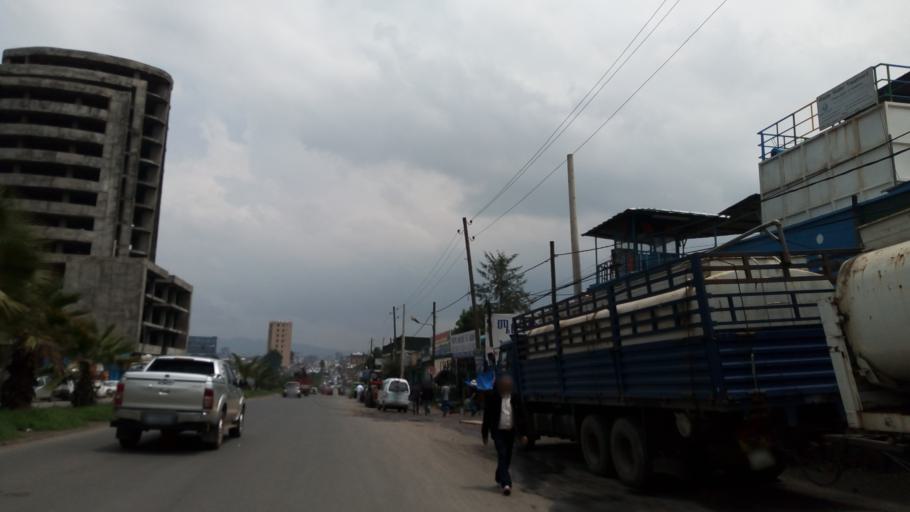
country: ET
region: Adis Abeba
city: Addis Ababa
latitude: 8.9829
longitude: 38.7550
